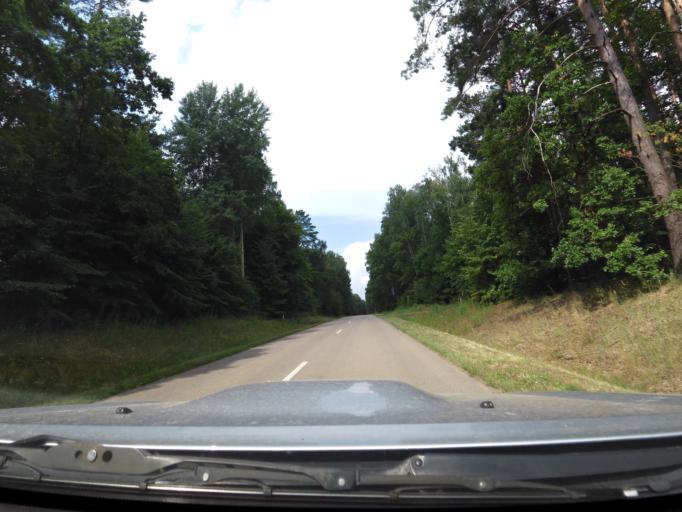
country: RU
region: Kaliningrad
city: Neman
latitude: 55.0887
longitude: 22.0368
